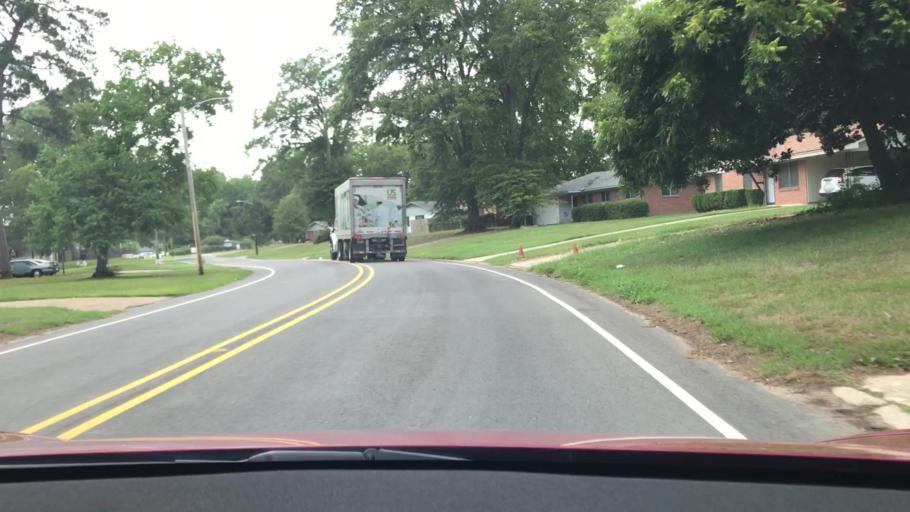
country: US
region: Louisiana
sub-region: De Soto Parish
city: Stonewall
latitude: 32.3959
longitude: -93.8021
